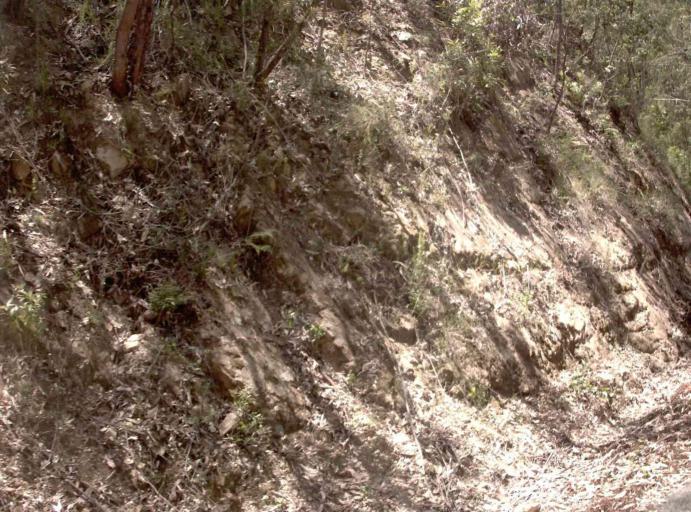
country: AU
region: New South Wales
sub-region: Bombala
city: Bombala
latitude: -37.4986
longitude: 148.9246
